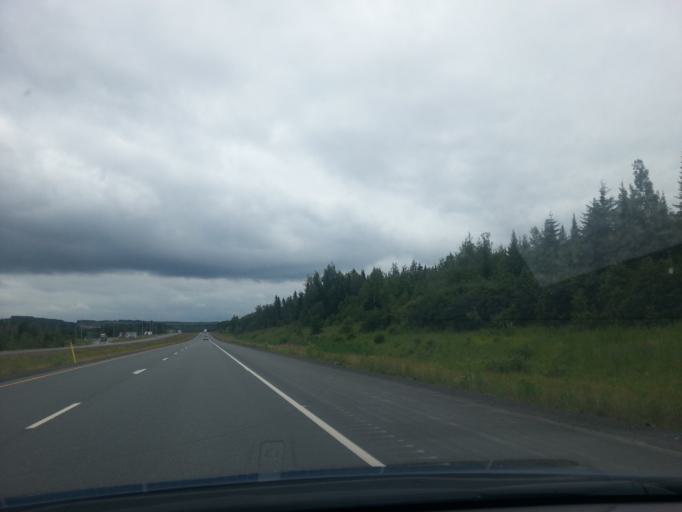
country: CA
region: New Brunswick
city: Harrison Brook
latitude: 47.2451
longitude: -67.9739
